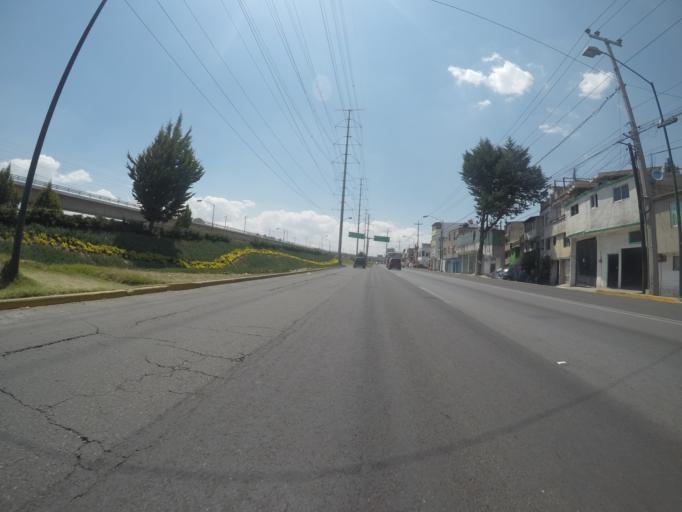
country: MX
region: Mexico
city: Toluca
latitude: 19.2689
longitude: -99.6498
